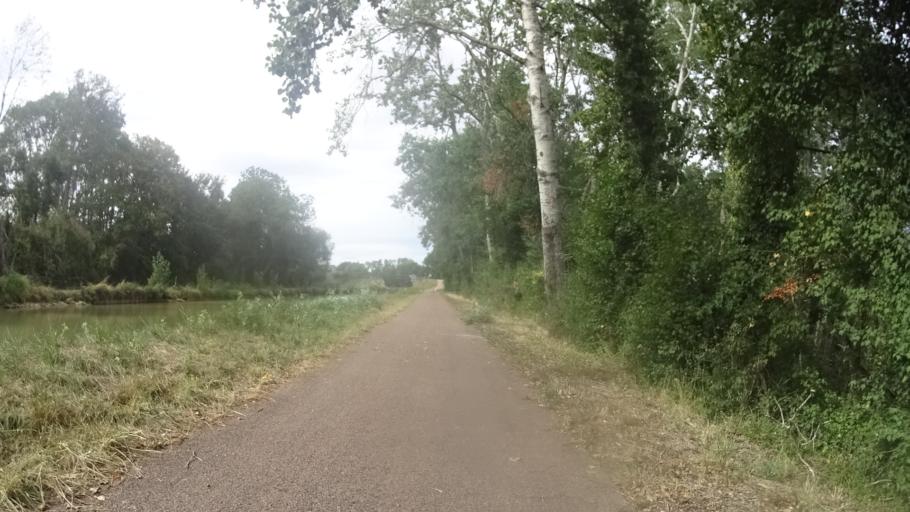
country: FR
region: Bourgogne
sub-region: Departement de la Nievre
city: Sermoise-sur-Loire
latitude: 46.9576
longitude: 3.1987
